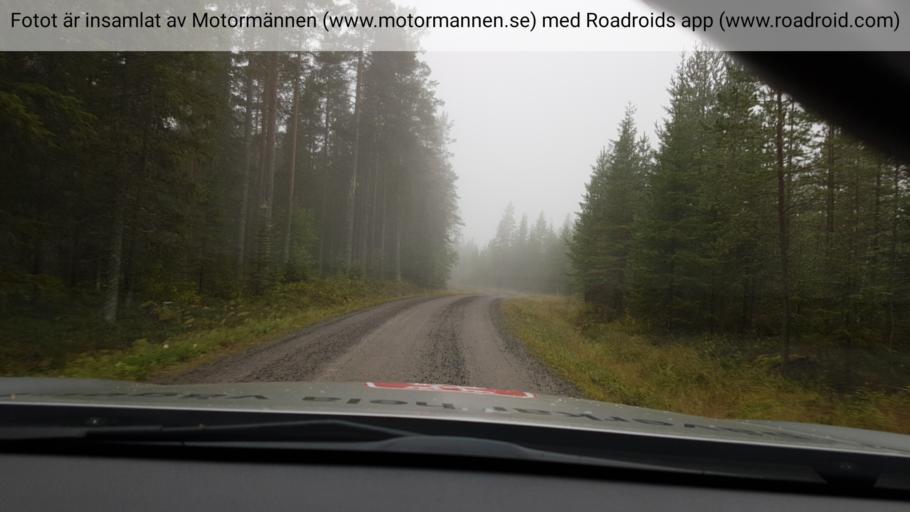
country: SE
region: Vaesterbotten
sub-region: Skelleftea Kommun
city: Burtraesk
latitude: 64.2512
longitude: 20.5672
